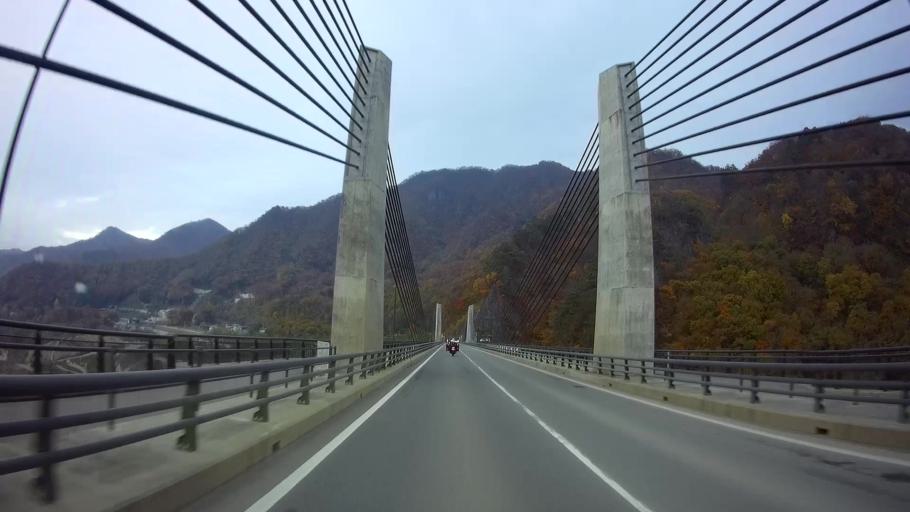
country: JP
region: Gunma
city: Nakanojomachi
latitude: 36.5452
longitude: 138.6877
